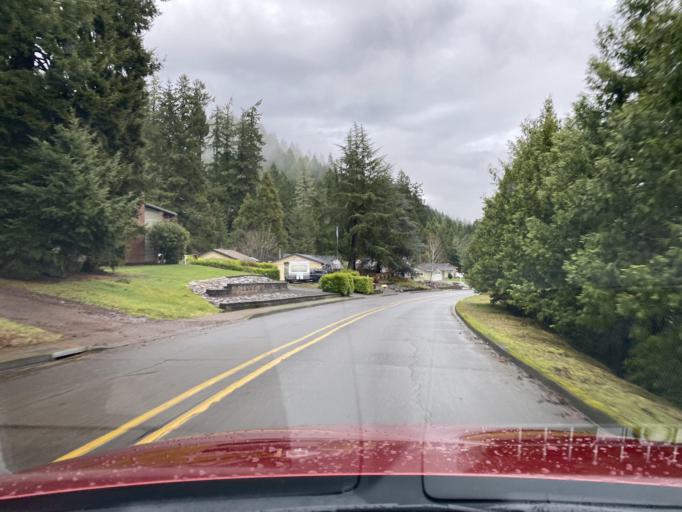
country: US
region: Oregon
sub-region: Lane County
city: Oakridge
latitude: 43.7519
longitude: -122.4845
